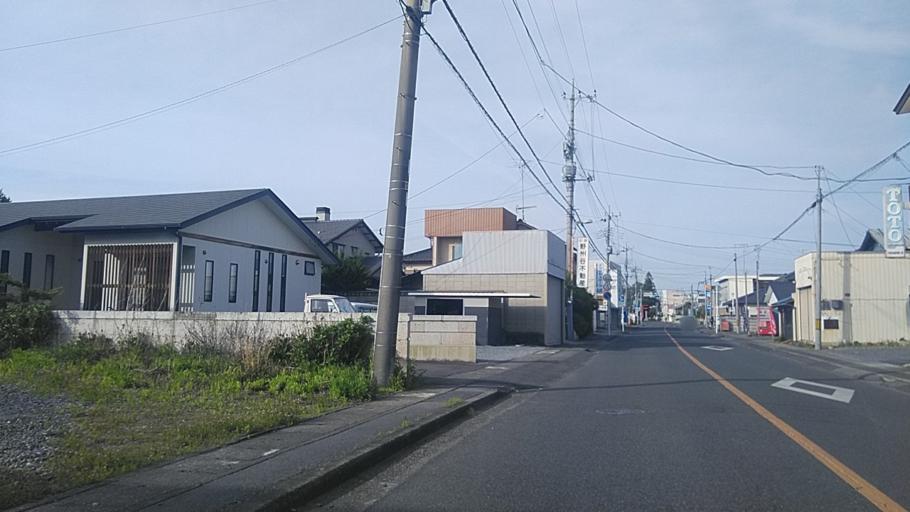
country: JP
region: Tochigi
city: Tanuma
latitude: 36.3648
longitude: 139.5775
